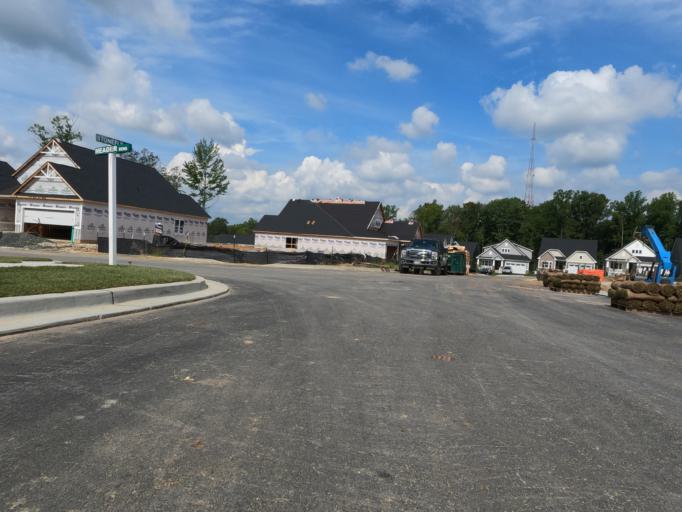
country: US
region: Maryland
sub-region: Anne Arundel County
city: Crofton
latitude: 39.0270
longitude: -76.7343
